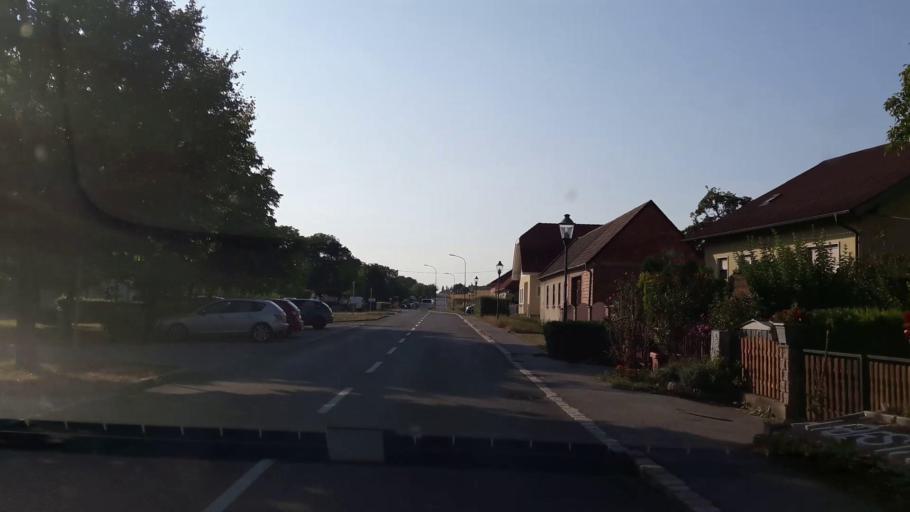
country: AT
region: Lower Austria
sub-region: Politischer Bezirk Ganserndorf
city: Orth an der Donau
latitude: 48.0686
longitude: 16.7029
